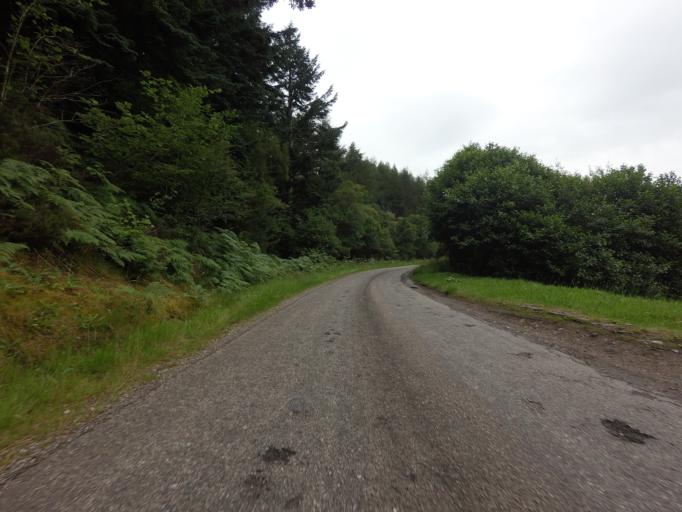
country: GB
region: Scotland
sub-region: Highland
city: Evanton
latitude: 57.9645
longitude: -4.4107
